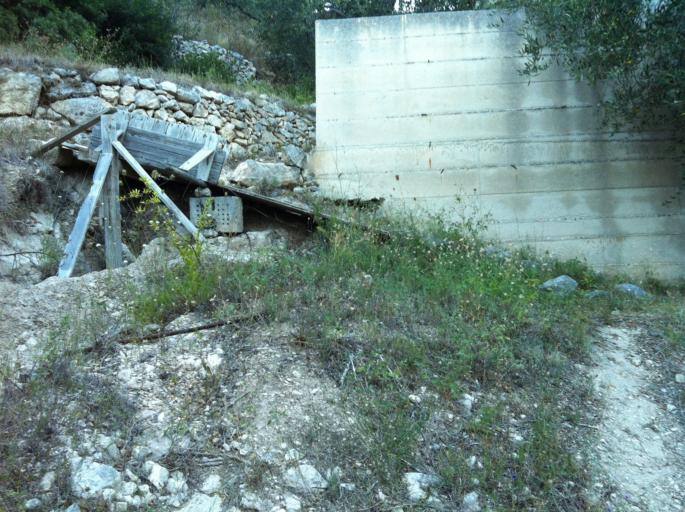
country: IT
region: Apulia
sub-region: Provincia di Foggia
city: Manfredonia
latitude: 41.6676
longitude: 15.9277
